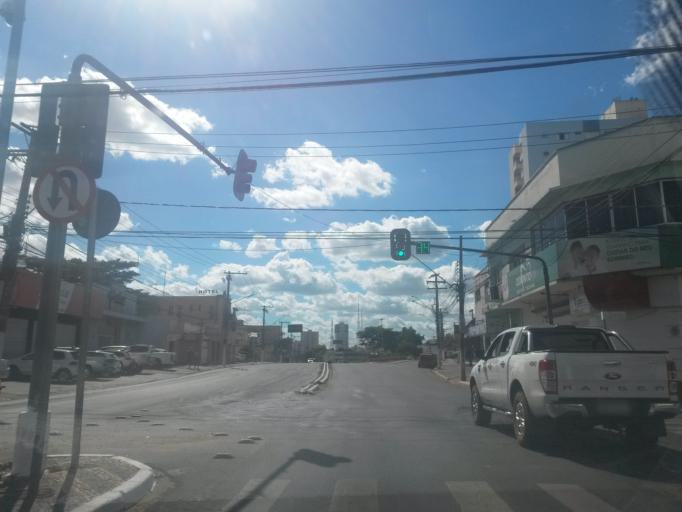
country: BR
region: Mato Grosso
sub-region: Cuiaba
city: Cuiaba
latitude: -15.5996
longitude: -56.0890
